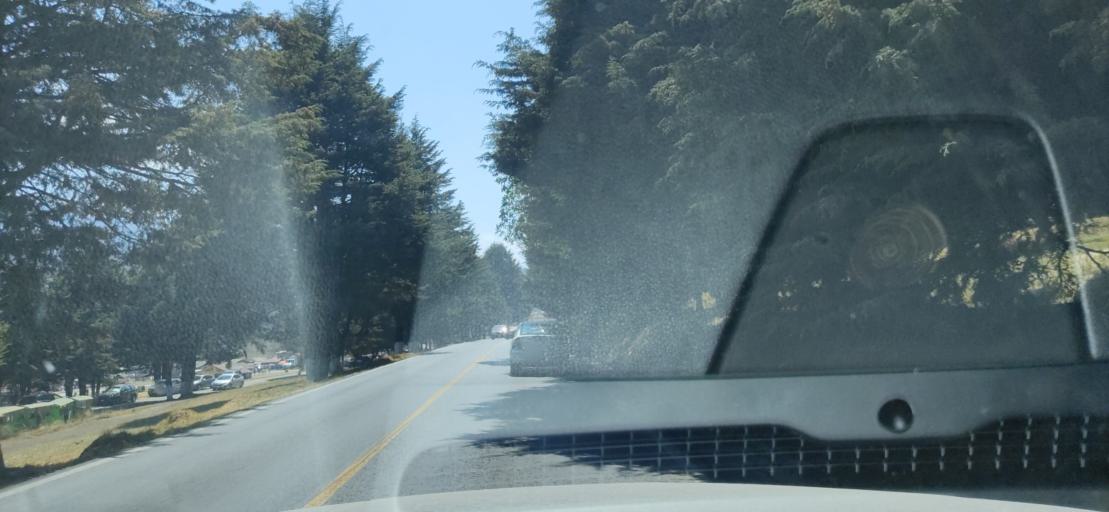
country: MX
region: Mexico
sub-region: Ocoyoacac
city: San Jeronimo Acazulco
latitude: 19.2884
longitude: -99.3738
